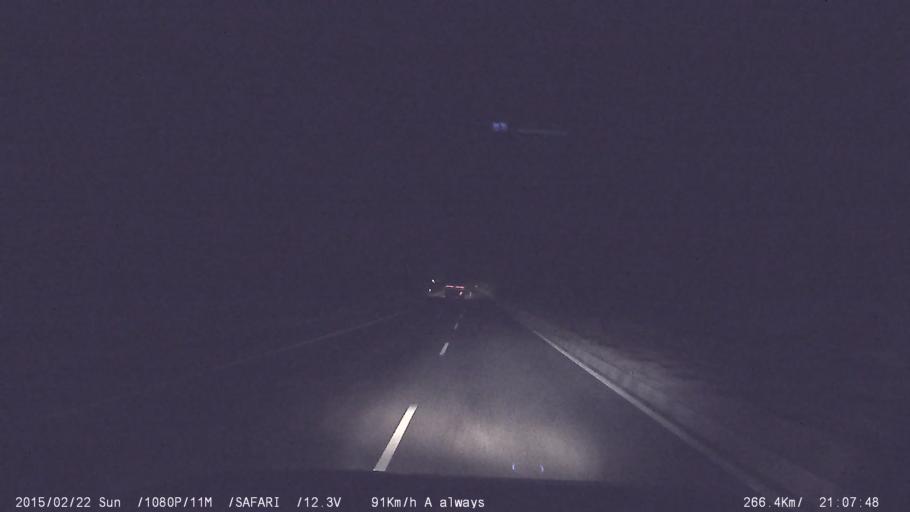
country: IN
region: Tamil Nadu
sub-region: Karur
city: Pallappatti
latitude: 10.7265
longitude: 77.9269
